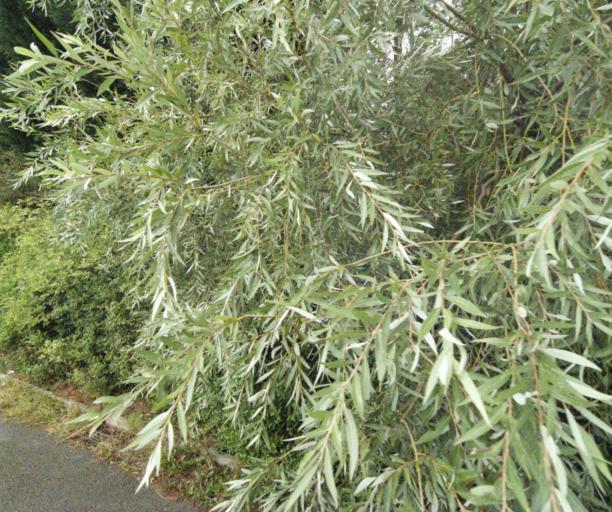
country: FR
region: Nord-Pas-de-Calais
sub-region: Departement du Nord
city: Lomme
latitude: 50.6383
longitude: 2.9860
